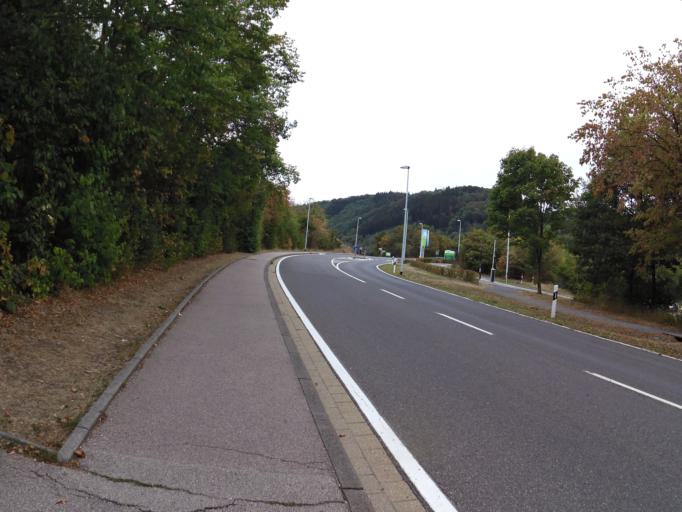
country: DE
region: North Rhine-Westphalia
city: Heimbach
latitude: 50.6338
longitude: 6.4439
